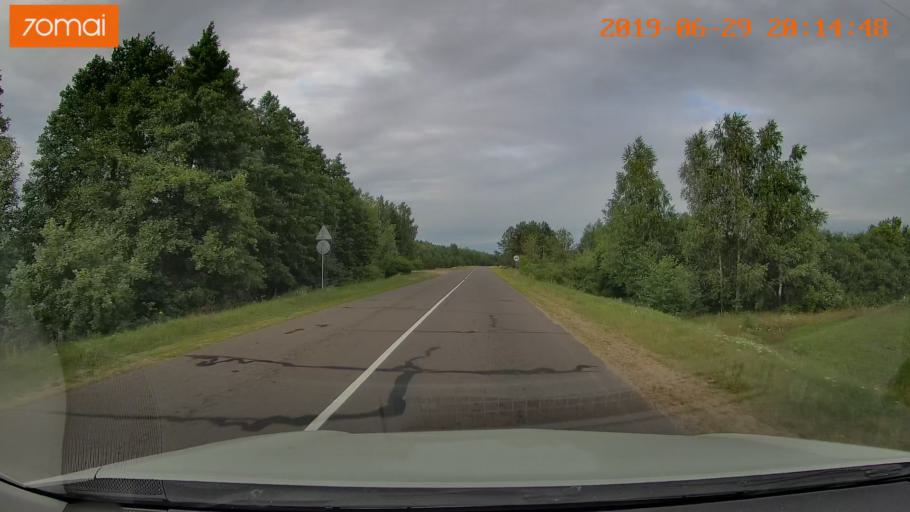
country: BY
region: Brest
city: Lahishyn
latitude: 52.3693
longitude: 26.1635
